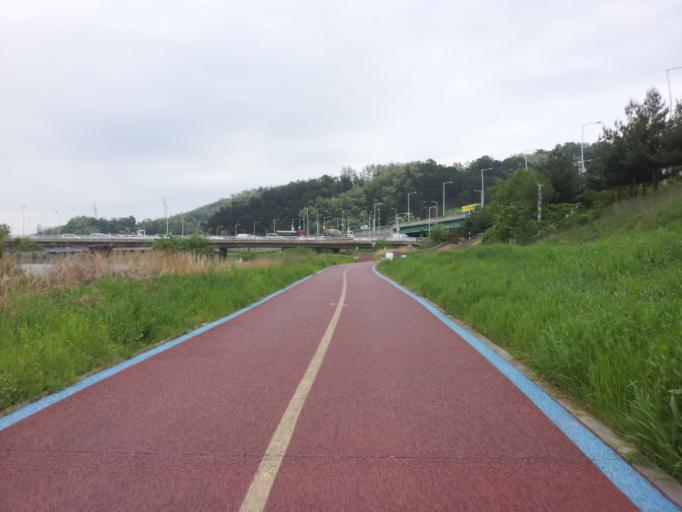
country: KR
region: Daejeon
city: Daejeon
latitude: 36.3769
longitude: 127.4092
